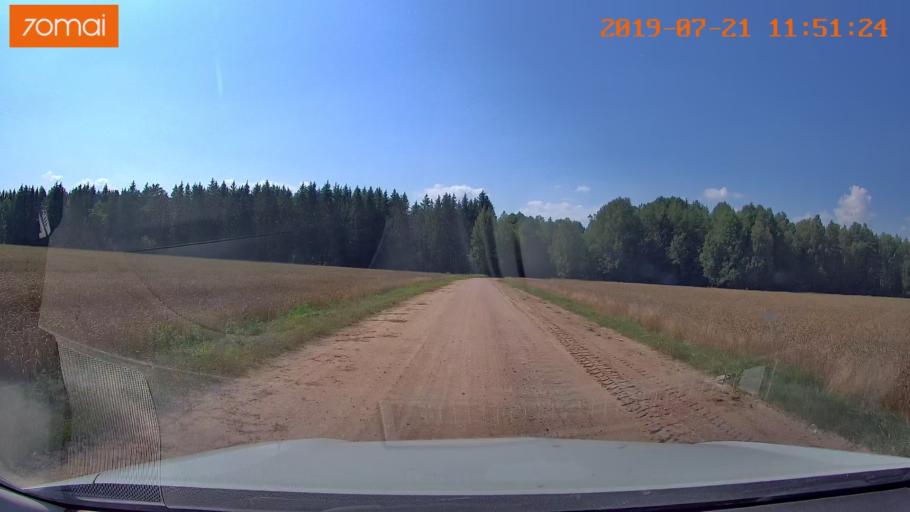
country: BY
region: Grodnenskaya
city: Lyubcha
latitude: 53.8837
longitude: 26.0129
